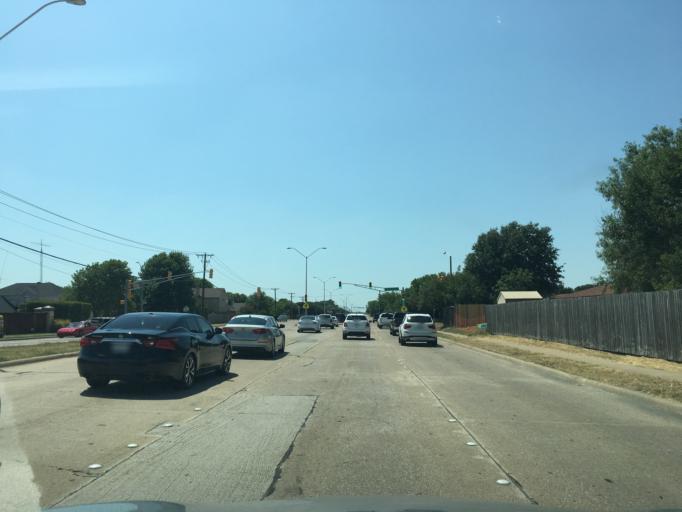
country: US
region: Texas
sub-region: Tarrant County
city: Edgecliff Village
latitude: 32.6350
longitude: -97.3567
